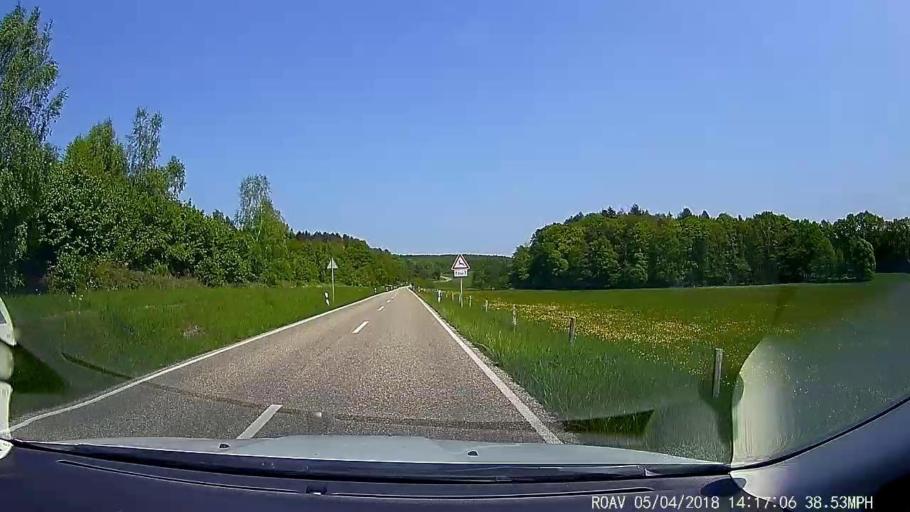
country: DE
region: Saarland
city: Saarwellingen
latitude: 49.3620
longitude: 6.8195
